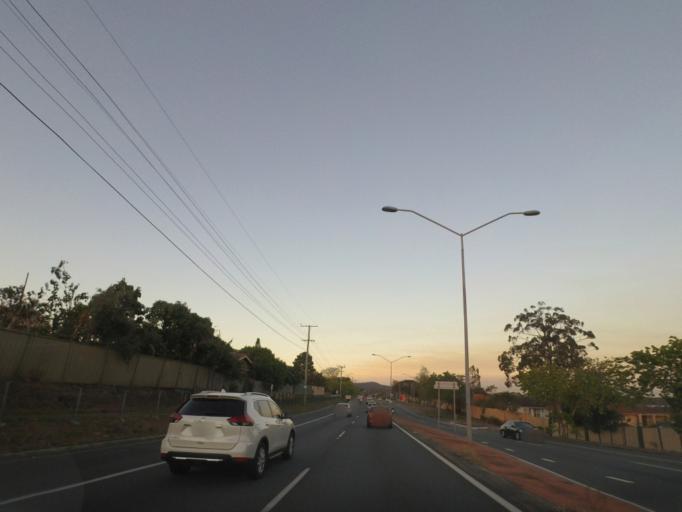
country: AU
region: Queensland
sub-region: Brisbane
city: Mansfield
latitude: -27.5518
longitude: 153.1043
